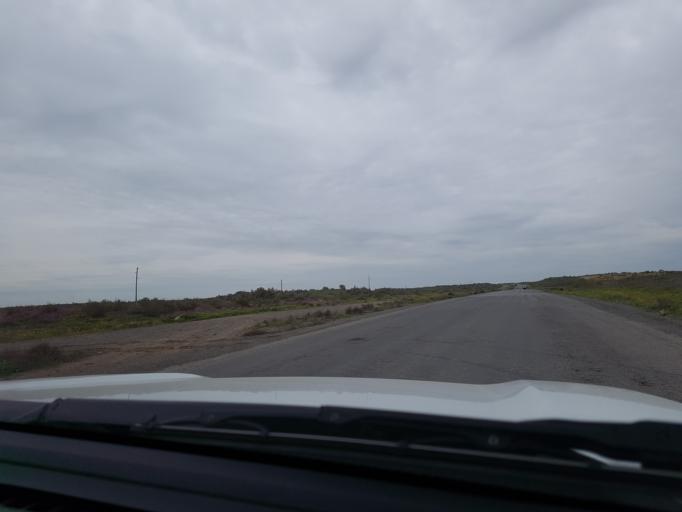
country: TM
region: Mary
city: Bayramaly
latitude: 37.9021
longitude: 62.6184
